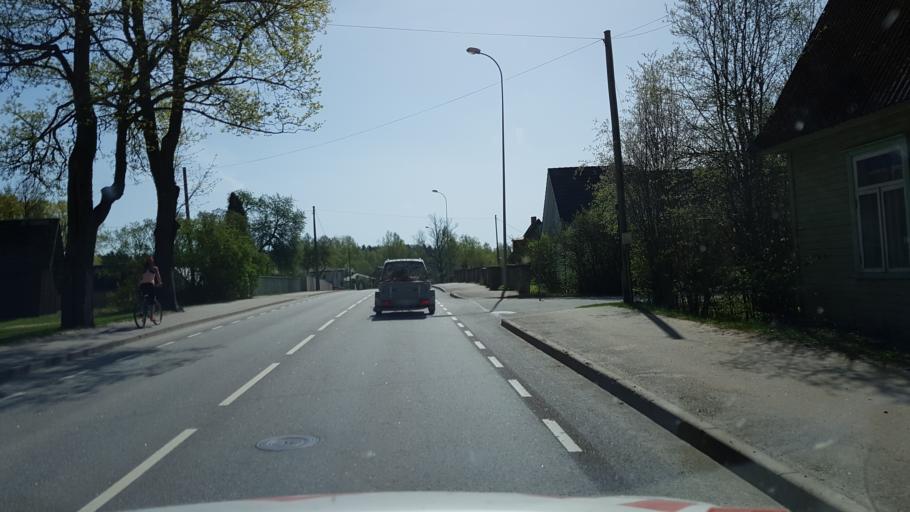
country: EE
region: Valgamaa
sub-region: Torva linn
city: Torva
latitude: 57.9996
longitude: 25.9302
